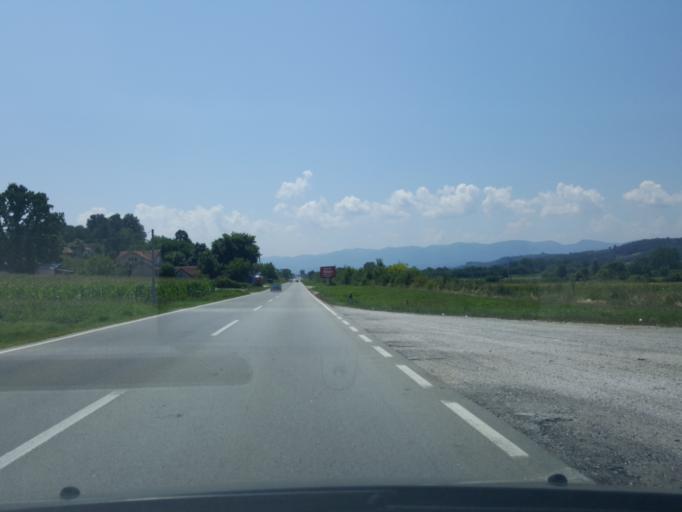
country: RS
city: Prislonica
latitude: 43.9475
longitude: 20.4145
